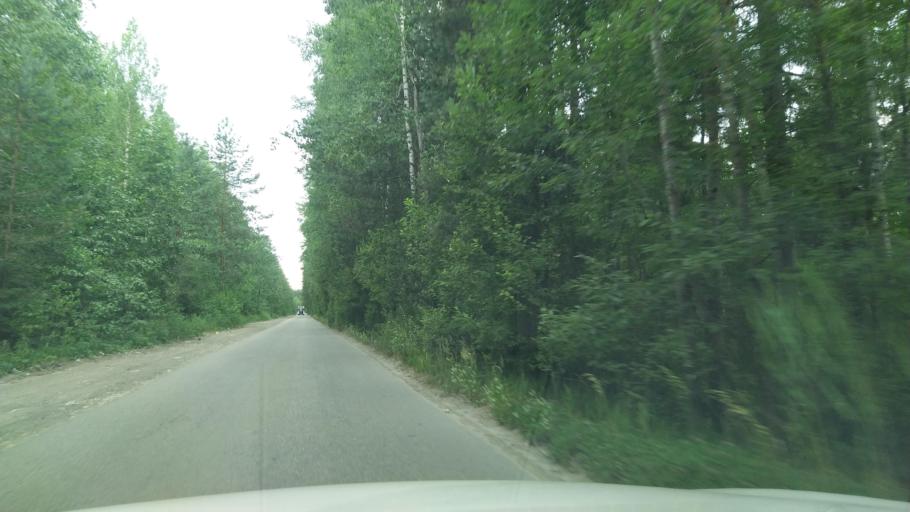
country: RU
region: St.-Petersburg
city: Bol'shaya Izhora
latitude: 59.9166
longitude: 29.5681
